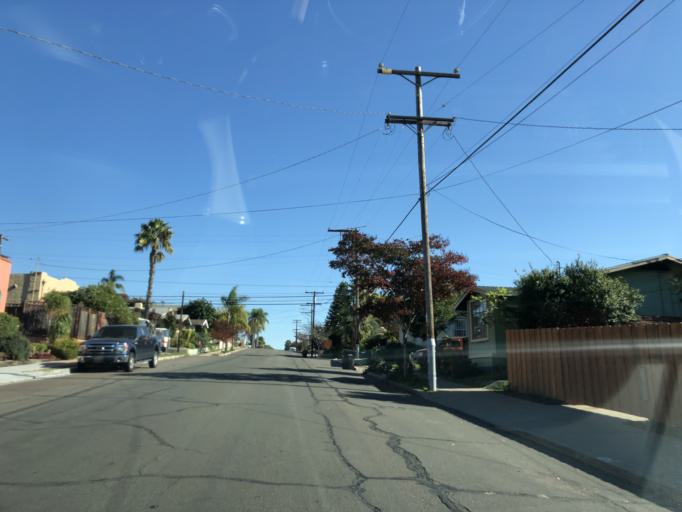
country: US
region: California
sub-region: San Diego County
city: San Diego
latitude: 32.7234
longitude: -117.1327
